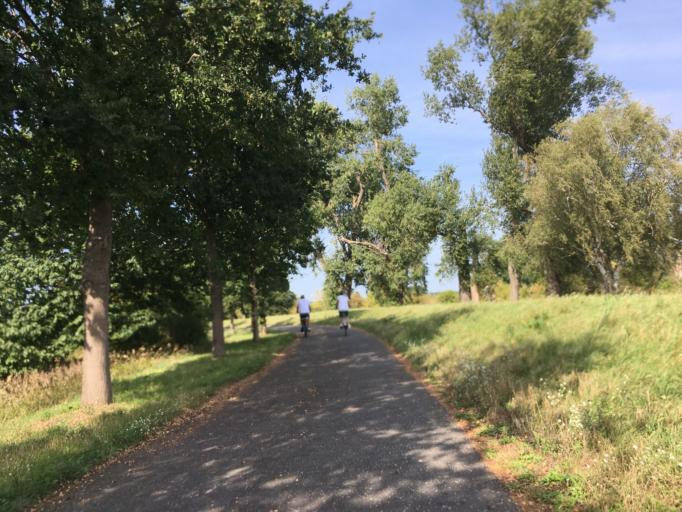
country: DE
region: Brandenburg
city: Guben
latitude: 51.9984
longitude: 14.7189
